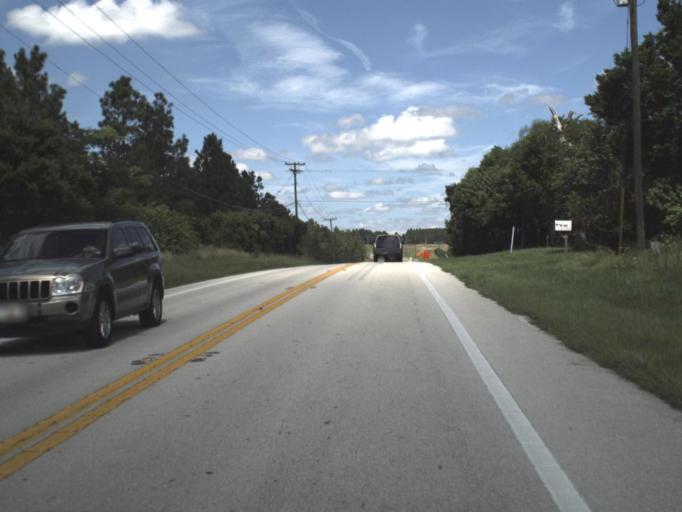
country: US
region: Florida
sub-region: Polk County
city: Lake Hamilton
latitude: 28.0762
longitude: -81.6201
